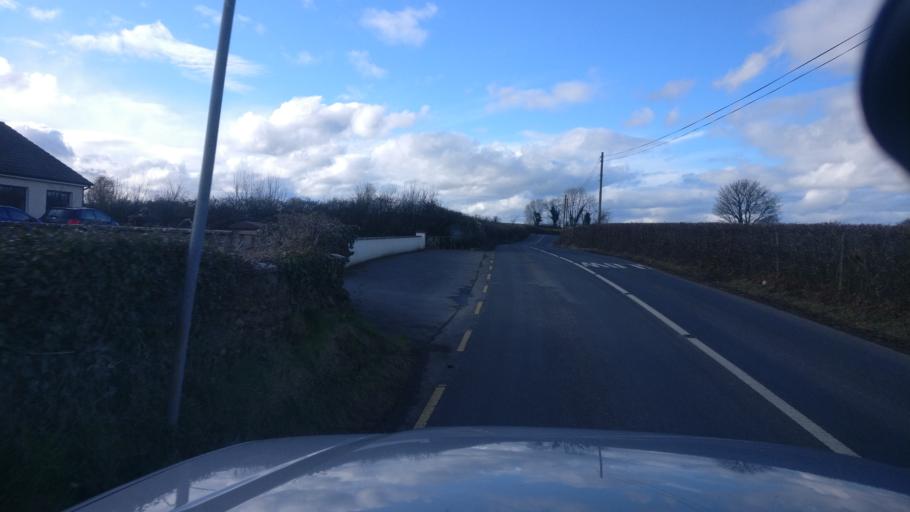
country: IE
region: Connaught
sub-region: County Galway
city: Loughrea
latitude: 53.1658
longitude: -8.3880
